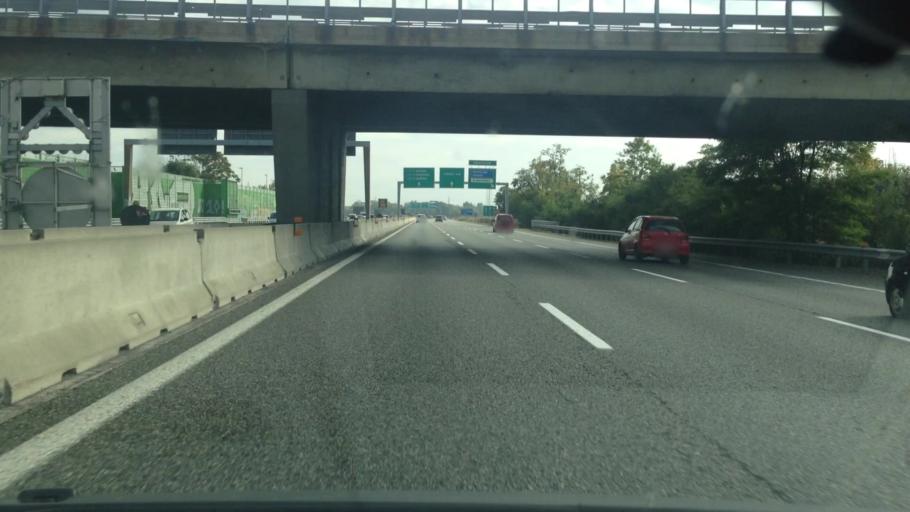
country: IT
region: Piedmont
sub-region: Provincia di Torino
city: Nichelino
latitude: 45.0025
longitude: 7.6225
